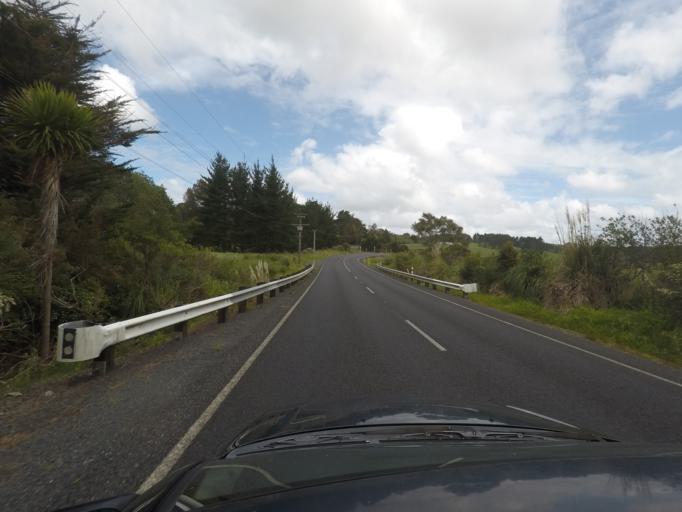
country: NZ
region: Auckland
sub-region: Auckland
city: Parakai
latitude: -36.6558
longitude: 174.5238
